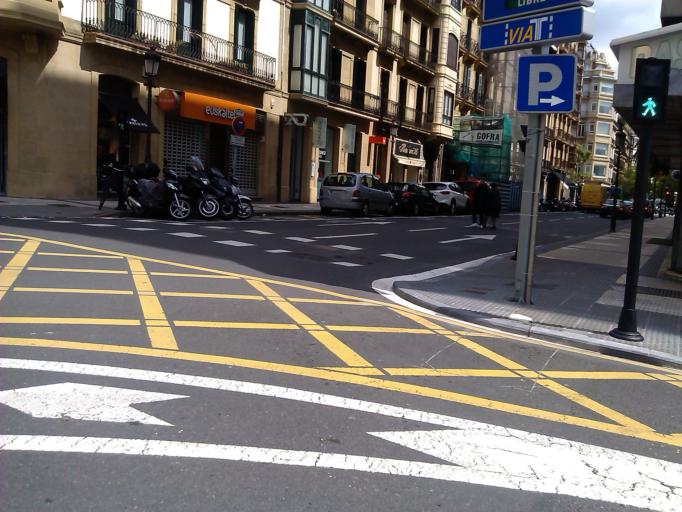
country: ES
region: Basque Country
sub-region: Provincia de Guipuzcoa
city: San Sebastian
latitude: 43.3200
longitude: -1.9839
